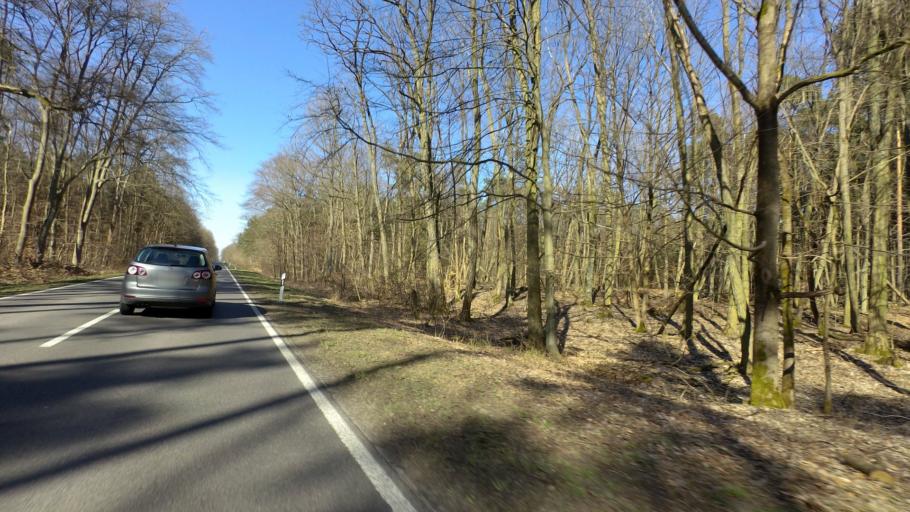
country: DE
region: Brandenburg
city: Eberswalde
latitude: 52.7950
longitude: 13.8373
